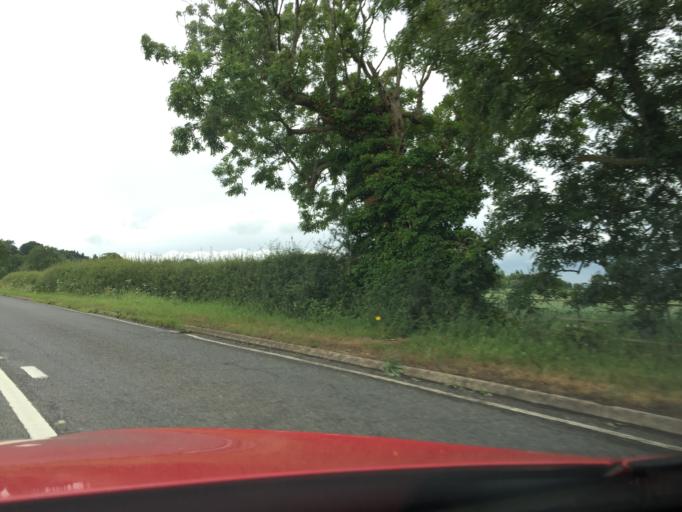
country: GB
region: England
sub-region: Warwickshire
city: Dunchurch
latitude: 52.2533
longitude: -1.2607
